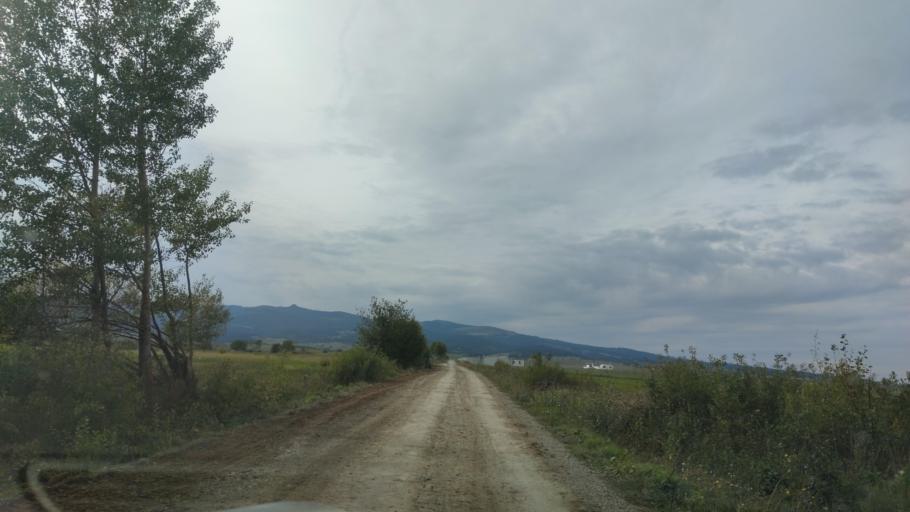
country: RO
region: Harghita
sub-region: Comuna Subcetate
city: Subcetate
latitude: 46.8168
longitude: 25.4154
